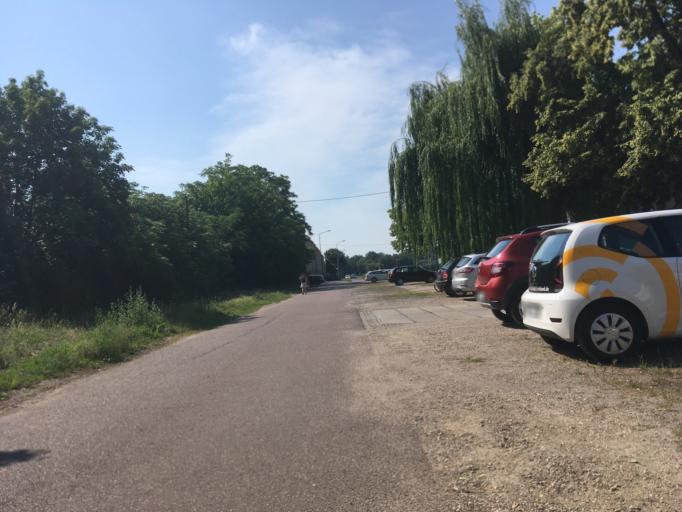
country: DE
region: Saxony-Anhalt
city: Dessau
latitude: 51.8190
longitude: 12.2368
